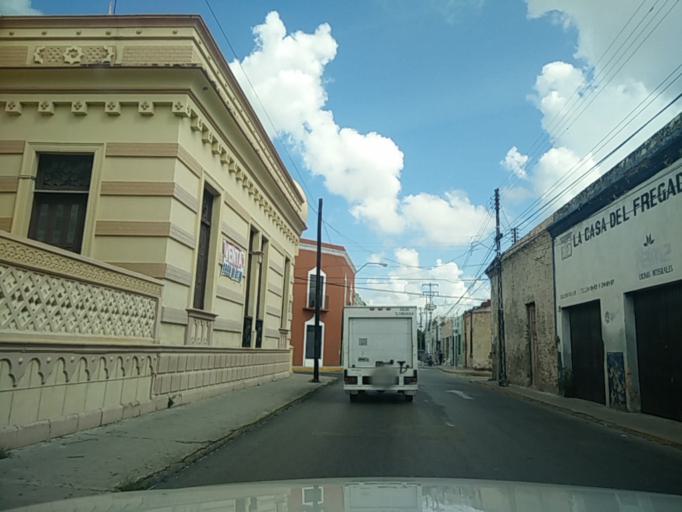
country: MX
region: Yucatan
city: Merida
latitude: 20.9724
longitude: -89.6196
